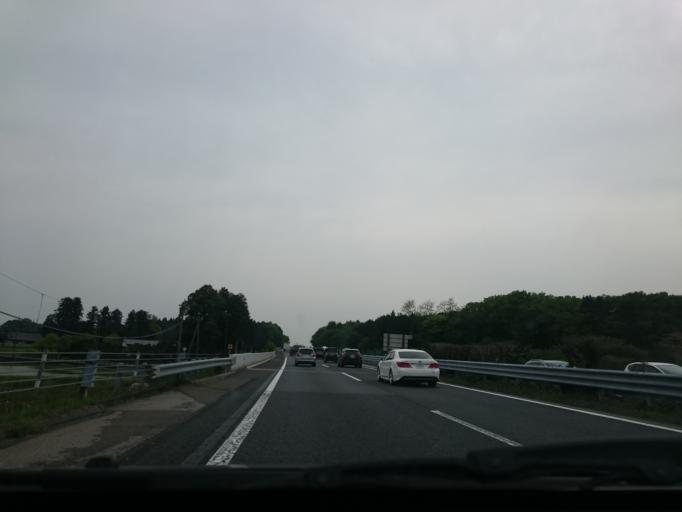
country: JP
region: Tochigi
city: Utsunomiya-shi
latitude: 36.6468
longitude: 139.8553
